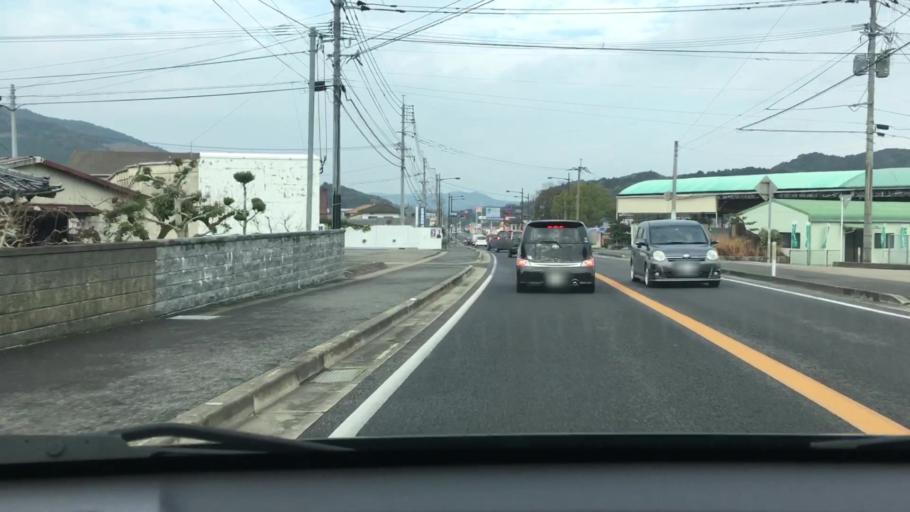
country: JP
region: Saga Prefecture
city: Imaricho-ko
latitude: 33.3118
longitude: 129.9284
